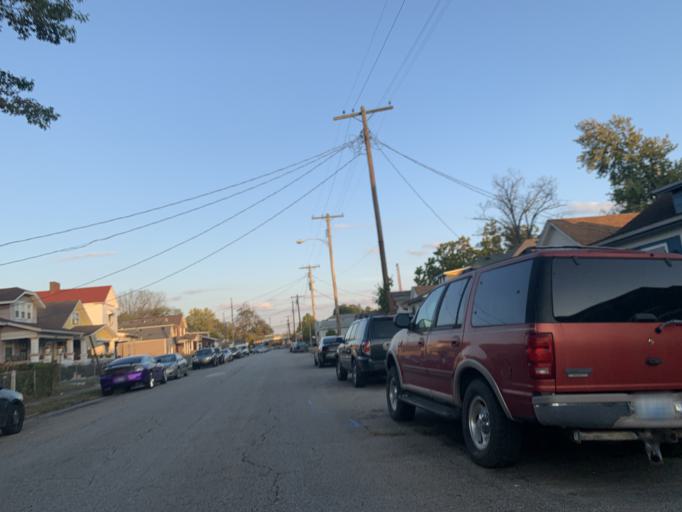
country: US
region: Indiana
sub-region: Floyd County
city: New Albany
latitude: 38.2557
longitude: -85.8088
